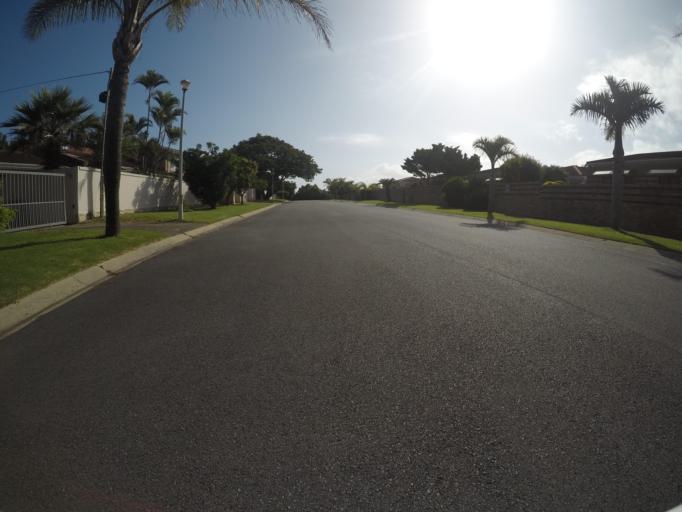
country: ZA
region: Eastern Cape
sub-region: Buffalo City Metropolitan Municipality
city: East London
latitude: -32.9741
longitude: 27.9557
